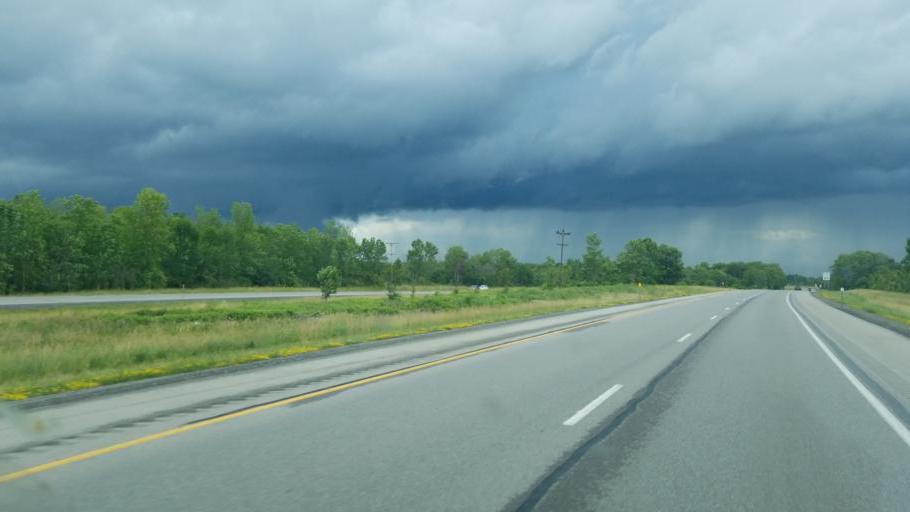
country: US
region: New York
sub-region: Erie County
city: Lake Erie Beach
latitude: 42.5927
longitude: -79.0486
